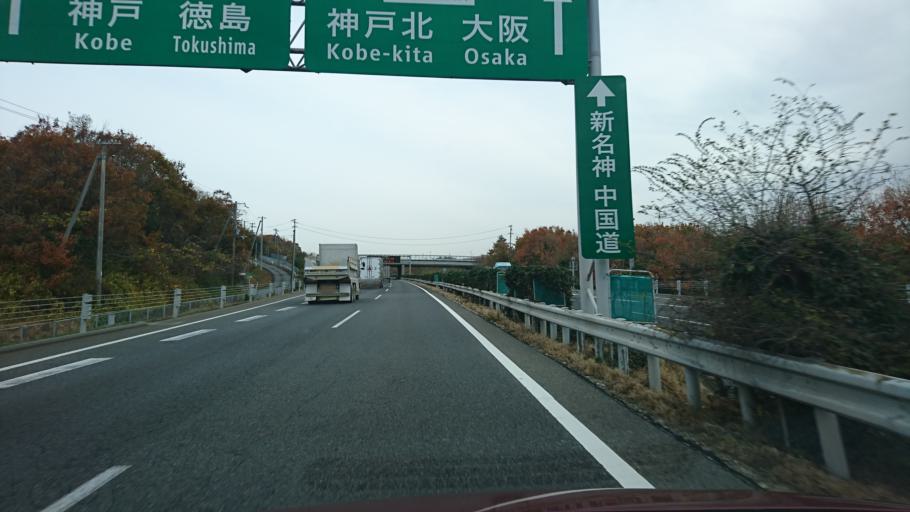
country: JP
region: Hyogo
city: Miki
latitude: 34.8009
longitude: 135.0655
